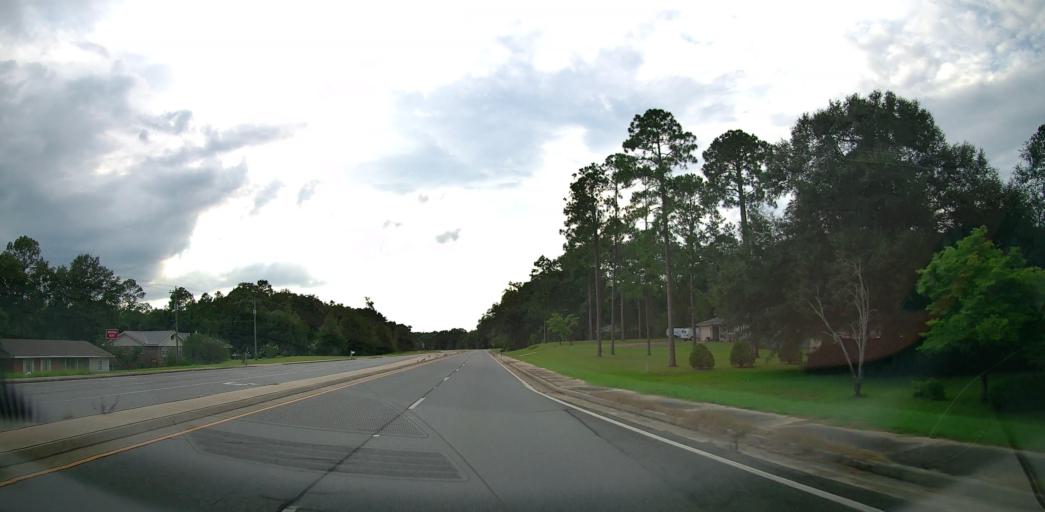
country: US
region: Georgia
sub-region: Pulaski County
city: Hawkinsville
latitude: 32.2796
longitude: -83.4297
